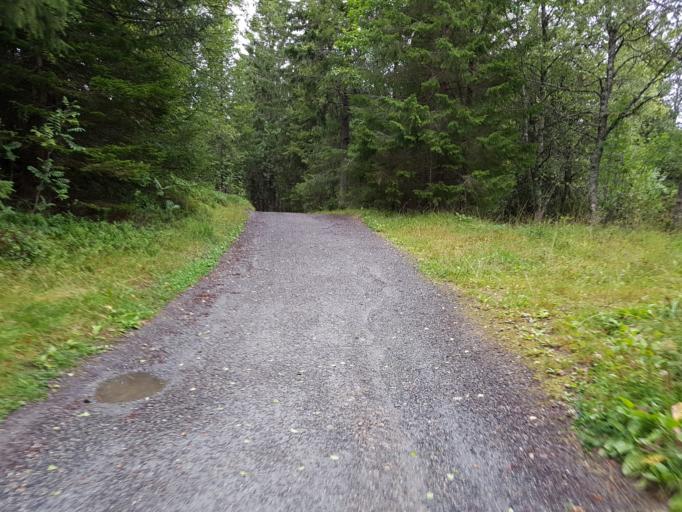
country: NO
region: Sor-Trondelag
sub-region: Trondheim
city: Trondheim
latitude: 63.3976
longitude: 10.4678
